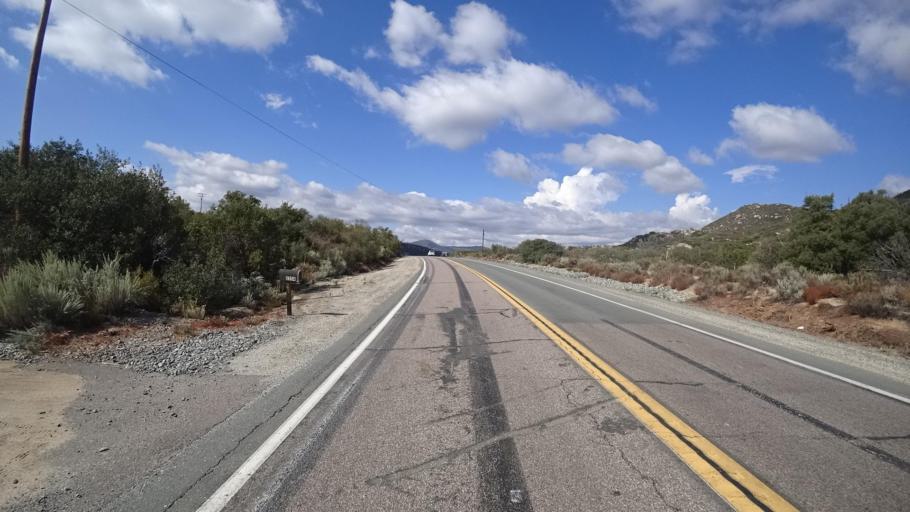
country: US
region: California
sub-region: San Diego County
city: Campo
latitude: 32.6876
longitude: -116.4885
